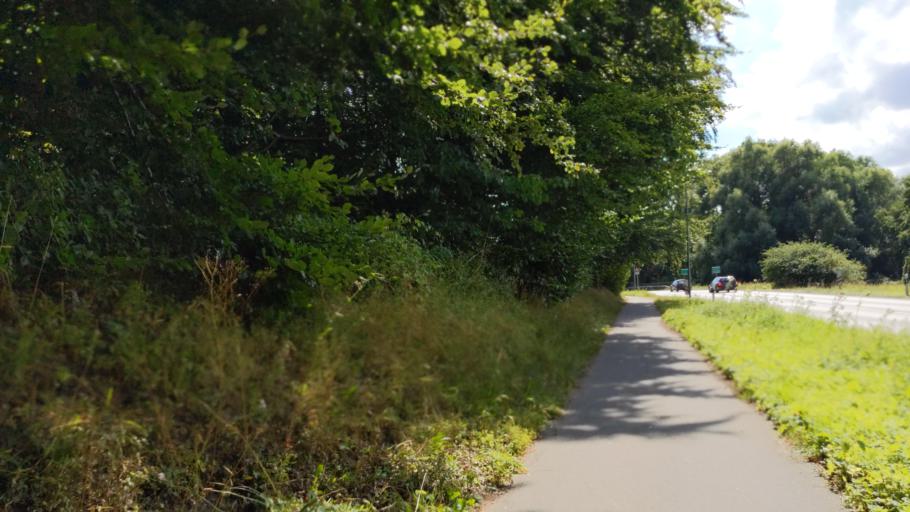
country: DE
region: Schleswig-Holstein
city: Ploen
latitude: 54.1514
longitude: 10.4026
